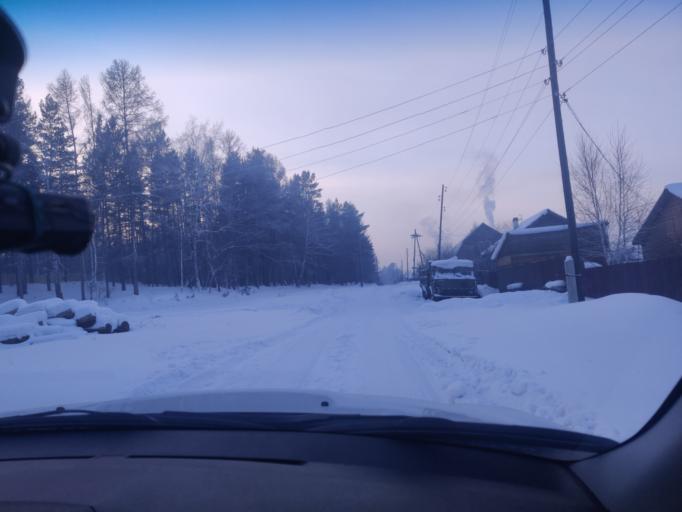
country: RU
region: Krasnoyarskiy
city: Boguchany
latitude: 58.3768
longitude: 97.4302
